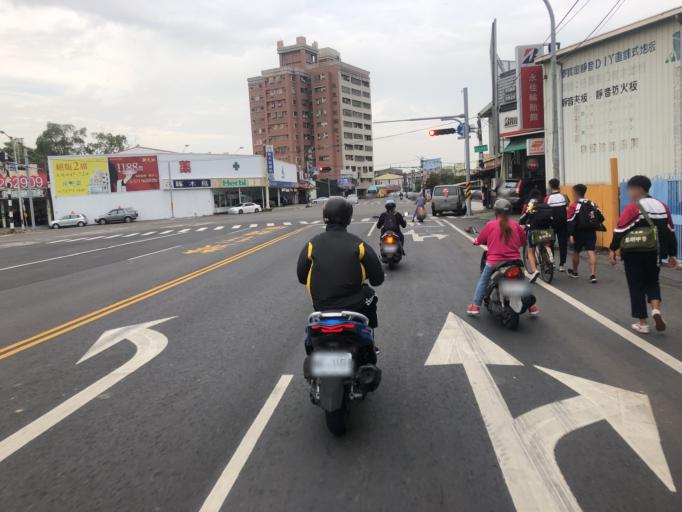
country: TW
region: Taiwan
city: Xinying
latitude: 23.1758
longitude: 120.2472
